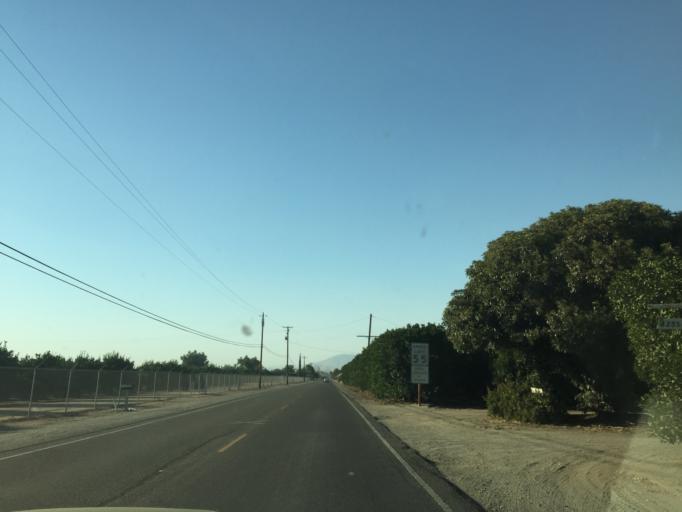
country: US
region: California
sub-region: Tulare County
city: Orosi
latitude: 36.5615
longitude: -119.2870
